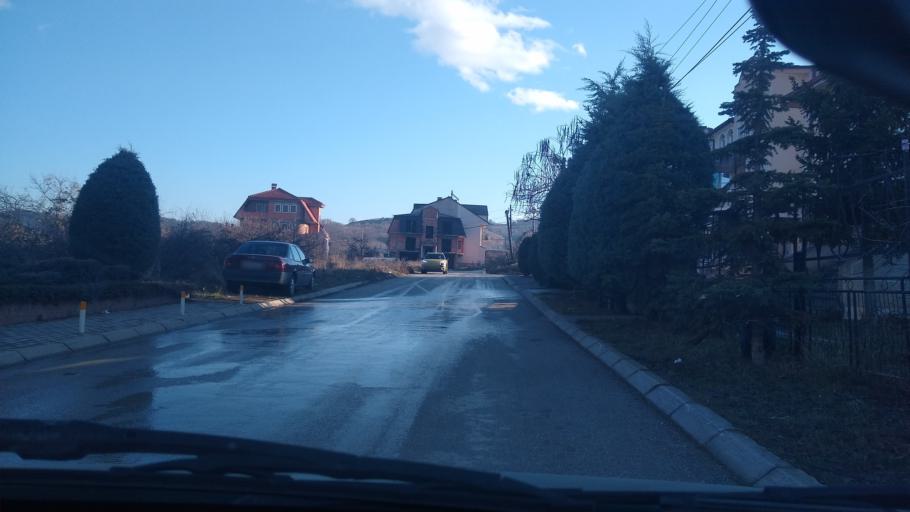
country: MK
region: Bitola
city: Bitola
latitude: 41.0209
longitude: 21.3159
